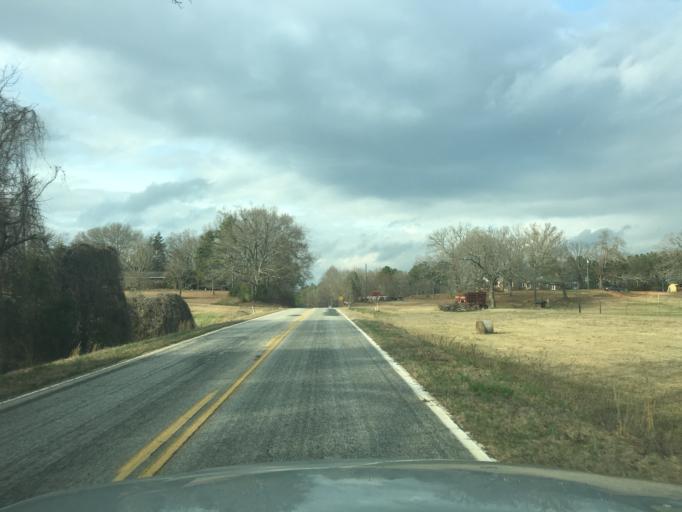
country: US
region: South Carolina
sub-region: Abbeville County
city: Due West
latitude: 34.2665
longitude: -82.4185
